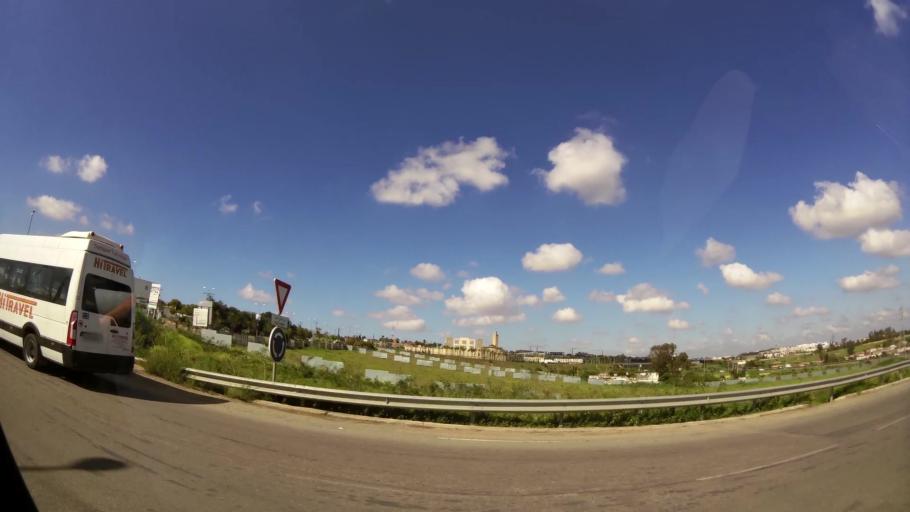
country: MA
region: Grand Casablanca
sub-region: Nouaceur
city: Bouskoura
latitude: 33.4844
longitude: -7.6354
